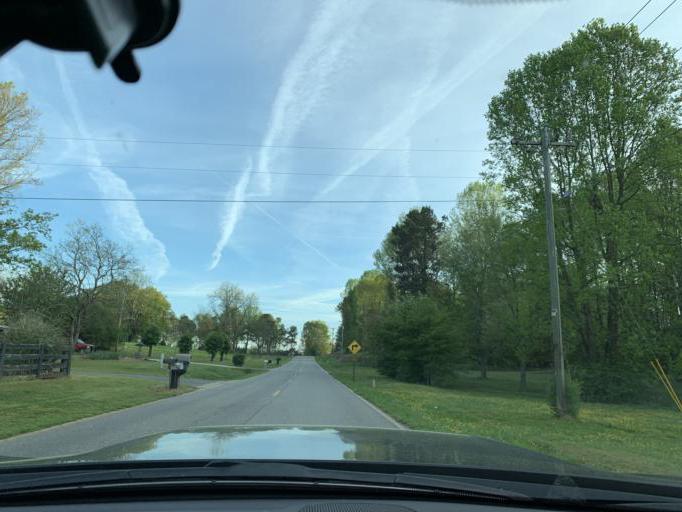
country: US
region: Georgia
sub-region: Forsyth County
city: Cumming
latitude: 34.2559
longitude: -84.1571
